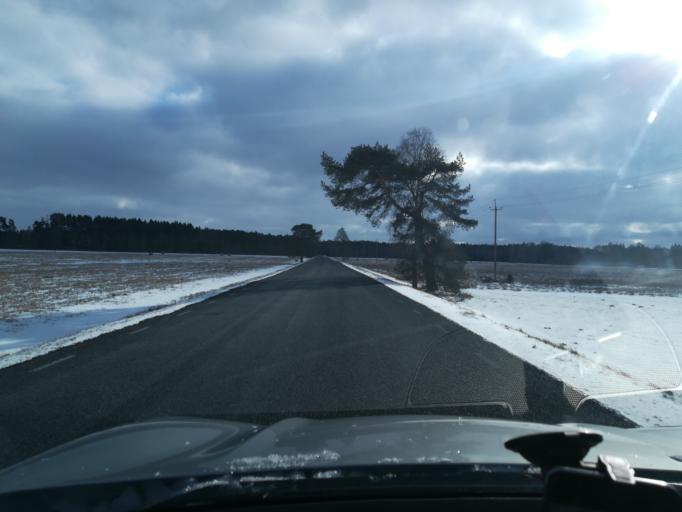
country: EE
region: Harju
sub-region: Keila linn
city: Keila
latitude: 59.4111
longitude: 24.4108
